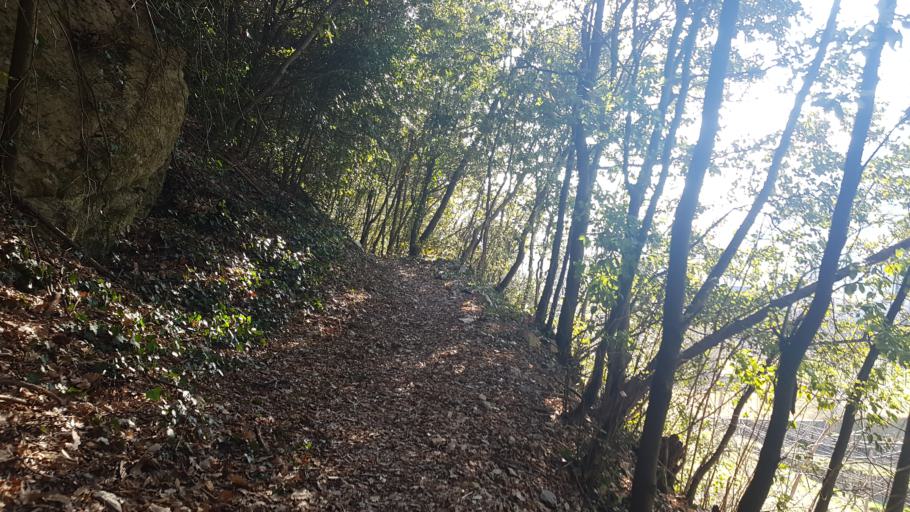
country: IT
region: Trentino-Alto Adige
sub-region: Provincia di Trento
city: Padergnone
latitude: 46.0705
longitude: 10.9864
